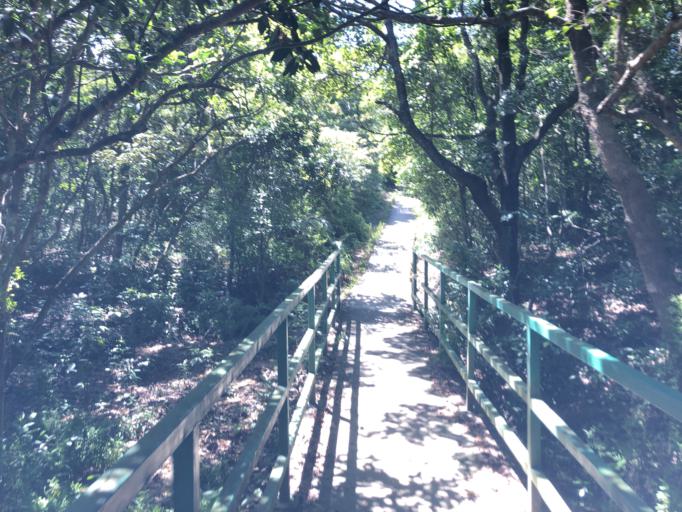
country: HK
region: Tuen Mun
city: Tuen Mun
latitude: 22.2811
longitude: 113.9841
